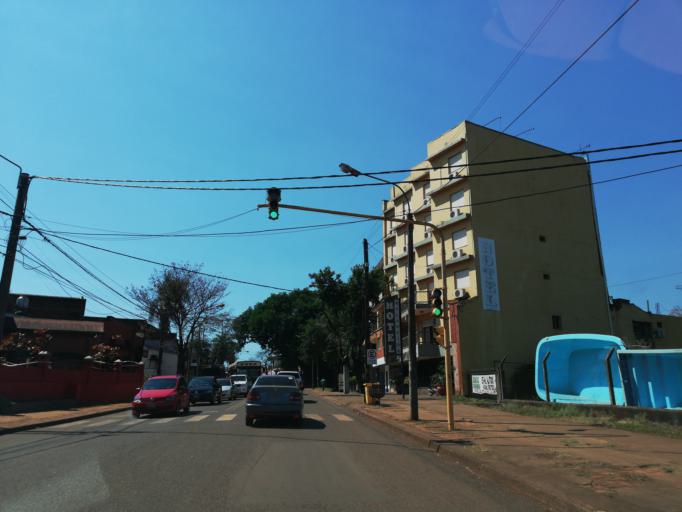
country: AR
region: Misiones
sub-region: Departamento de Eldorado
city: Eldorado
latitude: -26.4042
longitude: -54.6224
